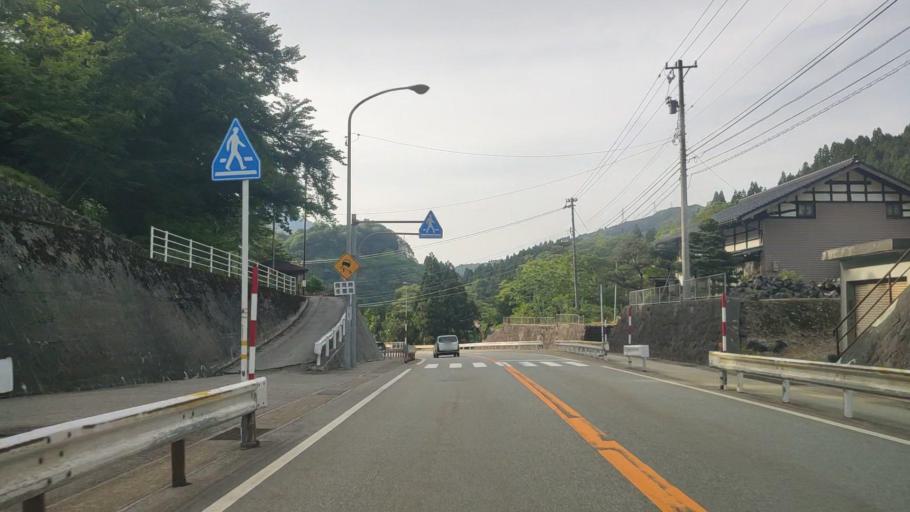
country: JP
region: Toyama
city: Yatsuomachi-higashikumisaka
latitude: 36.4578
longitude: 137.2507
